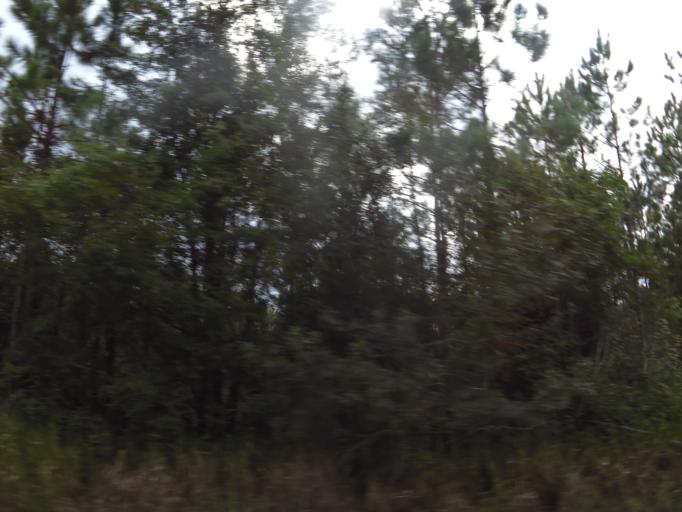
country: US
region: Florida
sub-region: Nassau County
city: Hilliard
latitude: 30.6033
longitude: -82.0668
